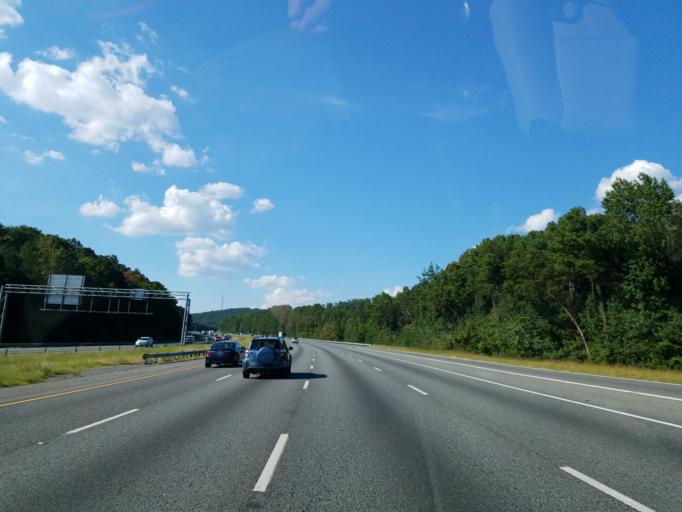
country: US
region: Georgia
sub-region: Bartow County
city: Cartersville
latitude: 34.1776
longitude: -84.7597
